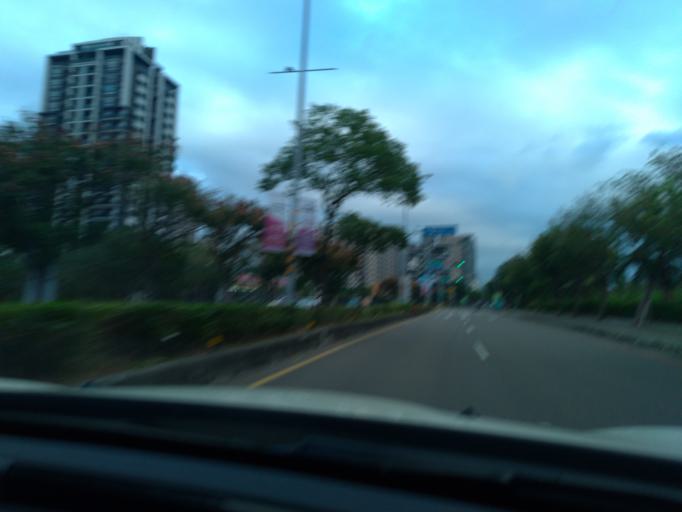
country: TW
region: Taiwan
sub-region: Hsinchu
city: Zhubei
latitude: 24.8045
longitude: 121.0292
